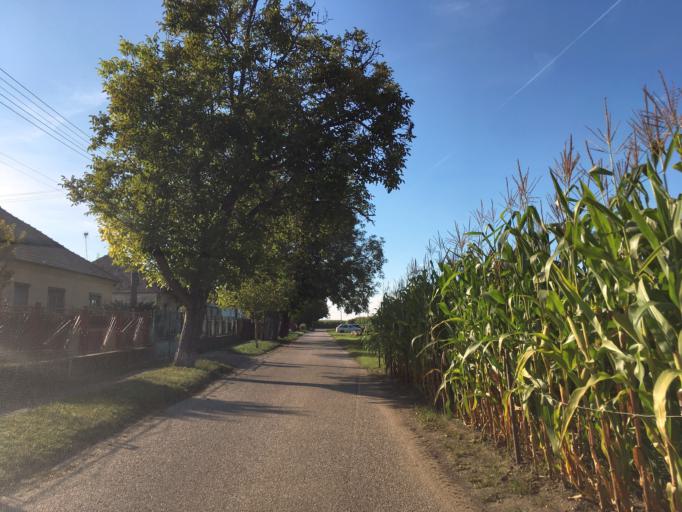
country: SK
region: Nitriansky
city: Svodin
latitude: 47.9009
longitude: 18.4136
